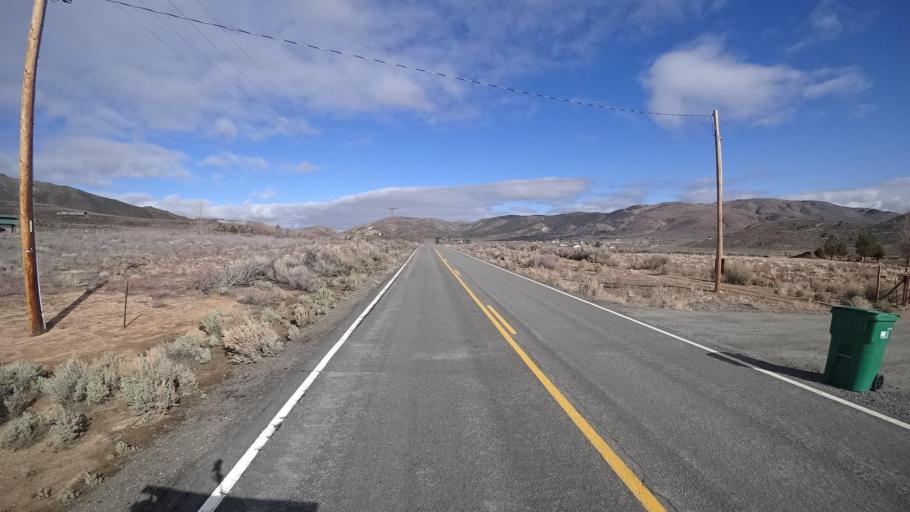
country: US
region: Nevada
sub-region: Washoe County
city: Cold Springs
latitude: 39.8775
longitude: -119.9655
